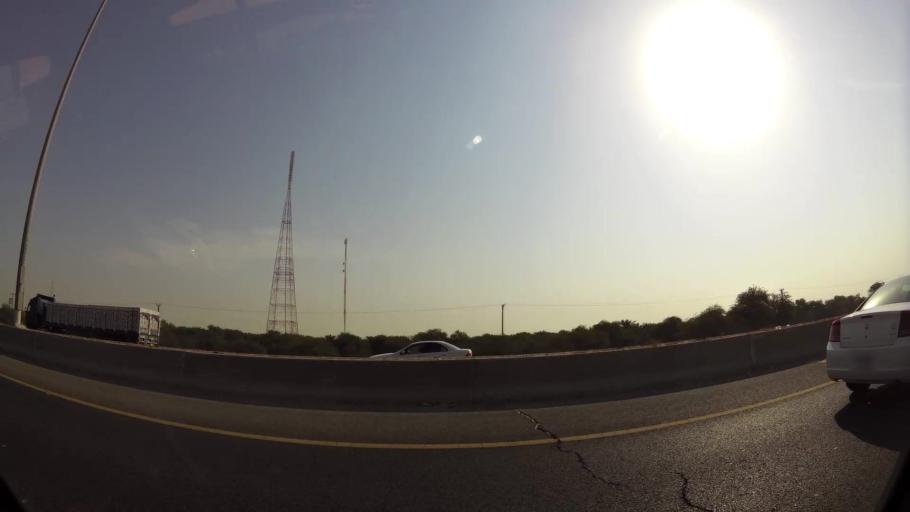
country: KW
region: Al Ahmadi
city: Al Ahmadi
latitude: 29.0782
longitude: 48.0997
